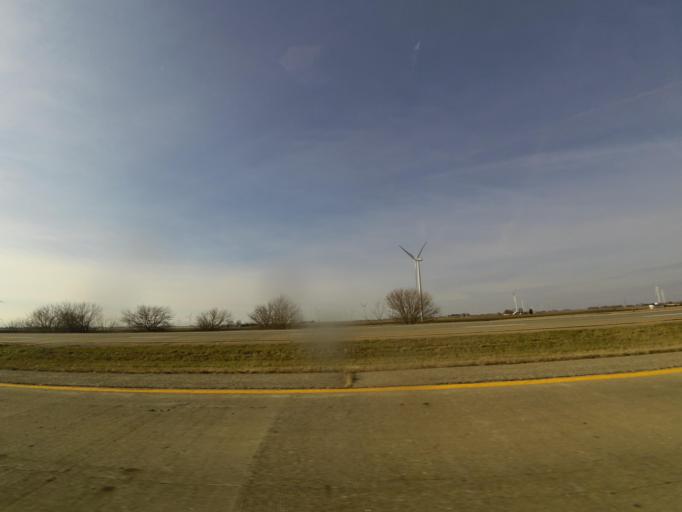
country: US
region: Illinois
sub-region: Macon County
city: Maroa
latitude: 40.0343
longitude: -88.9649
